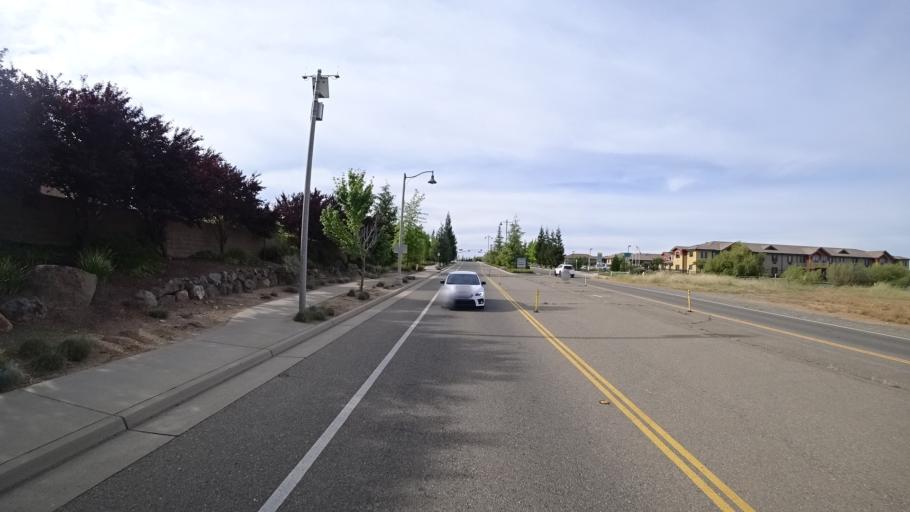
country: US
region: California
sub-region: Placer County
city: Lincoln
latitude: 38.8395
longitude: -121.2906
